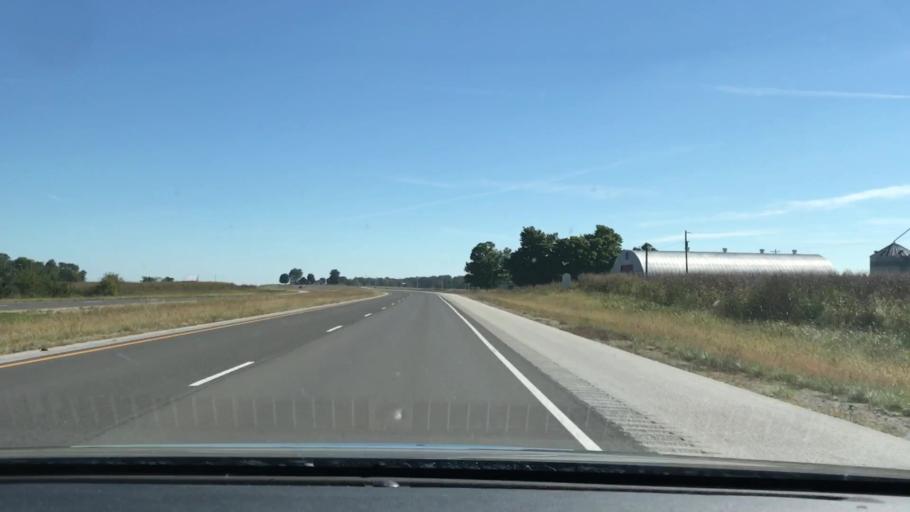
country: US
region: Kentucky
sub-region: Todd County
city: Elkton
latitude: 36.8055
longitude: -87.0565
